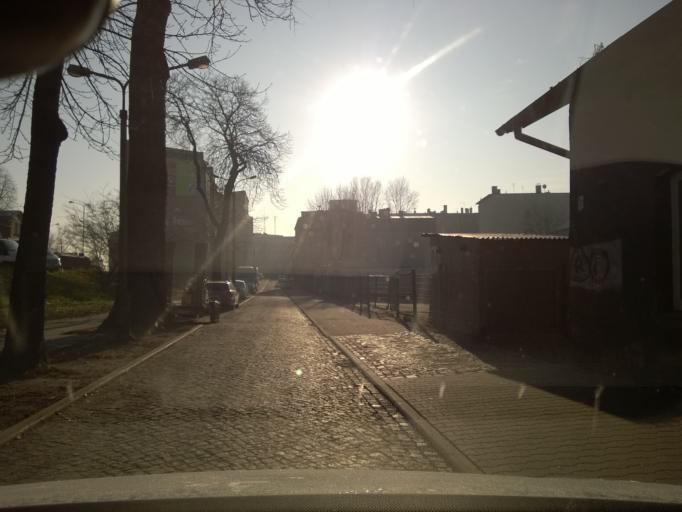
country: PL
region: Silesian Voivodeship
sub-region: Chorzow
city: Chorzow
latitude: 50.3052
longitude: 18.9505
